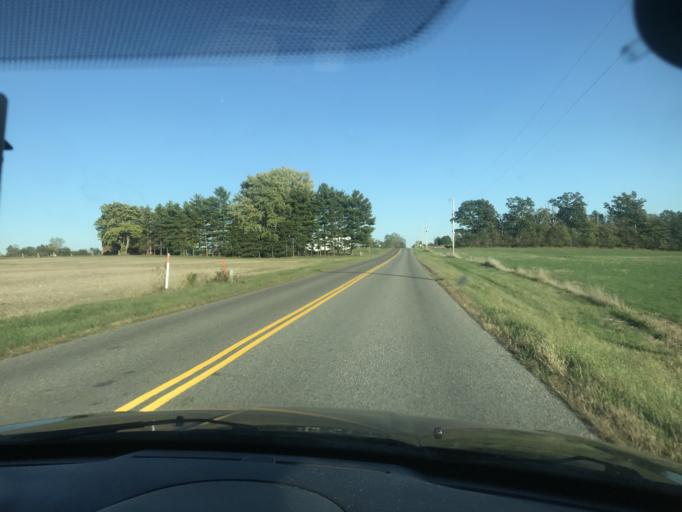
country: US
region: Ohio
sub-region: Logan County
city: De Graff
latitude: 40.3225
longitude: -83.8472
